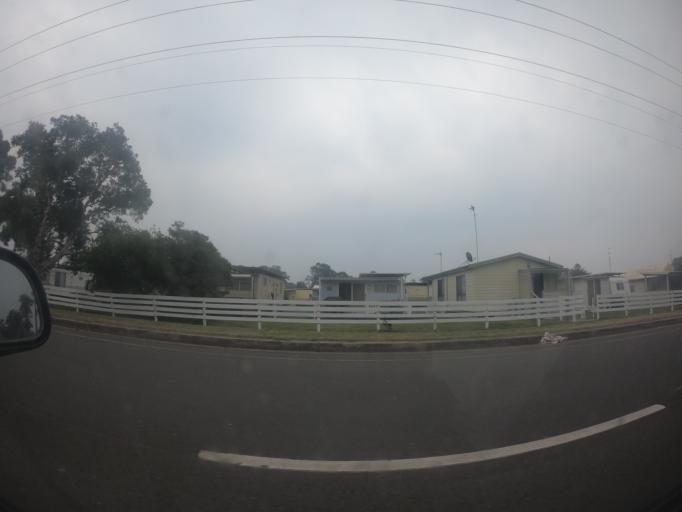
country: AU
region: New South Wales
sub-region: Shellharbour
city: Barrack Heights
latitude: -34.5663
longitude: 150.8668
